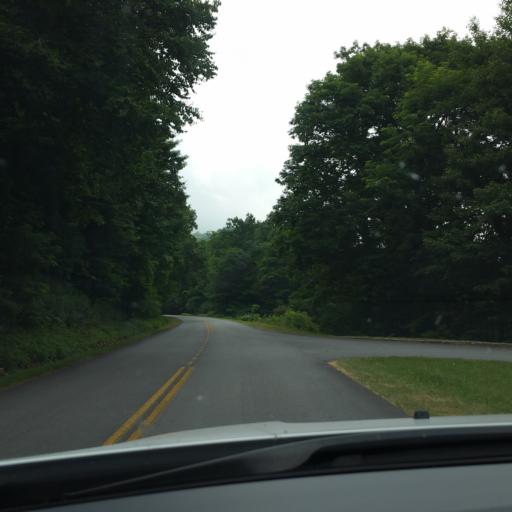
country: US
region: North Carolina
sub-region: Buncombe County
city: Bent Creek
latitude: 35.4474
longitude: -82.7172
